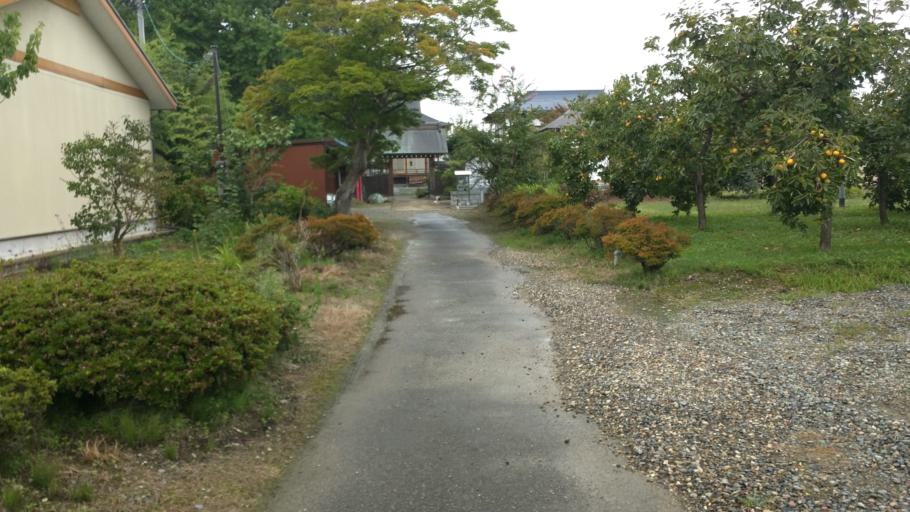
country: JP
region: Fukushima
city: Kitakata
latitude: 37.4951
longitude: 139.8739
